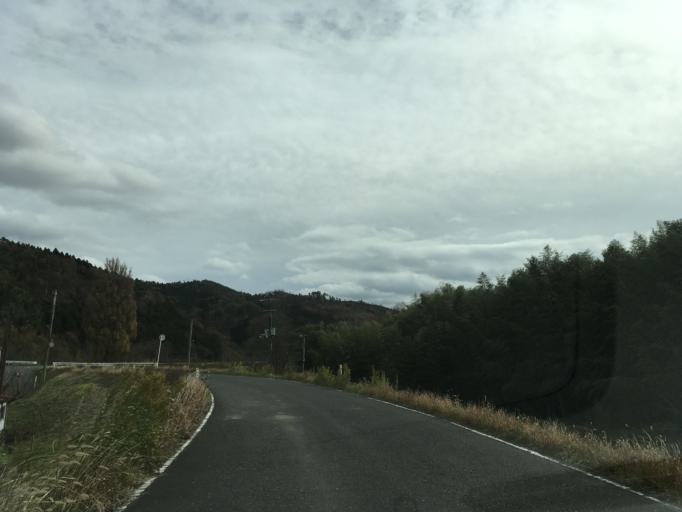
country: JP
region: Iwate
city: Ichinoseki
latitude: 38.7548
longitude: 141.2805
